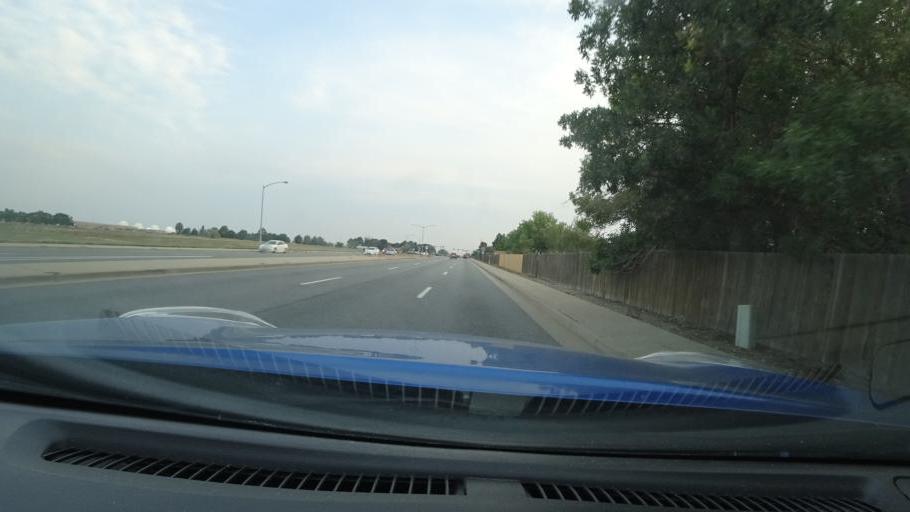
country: US
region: Colorado
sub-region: Adams County
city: Aurora
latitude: 39.7279
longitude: -104.7913
